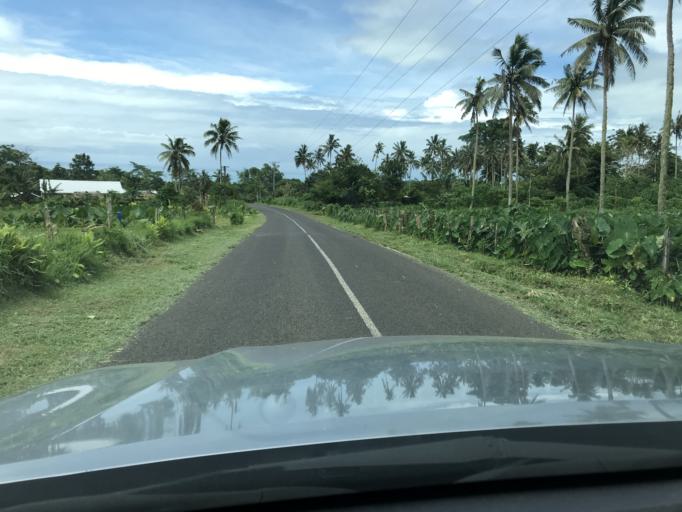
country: WS
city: Fasito`outa
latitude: -13.8683
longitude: -171.9125
